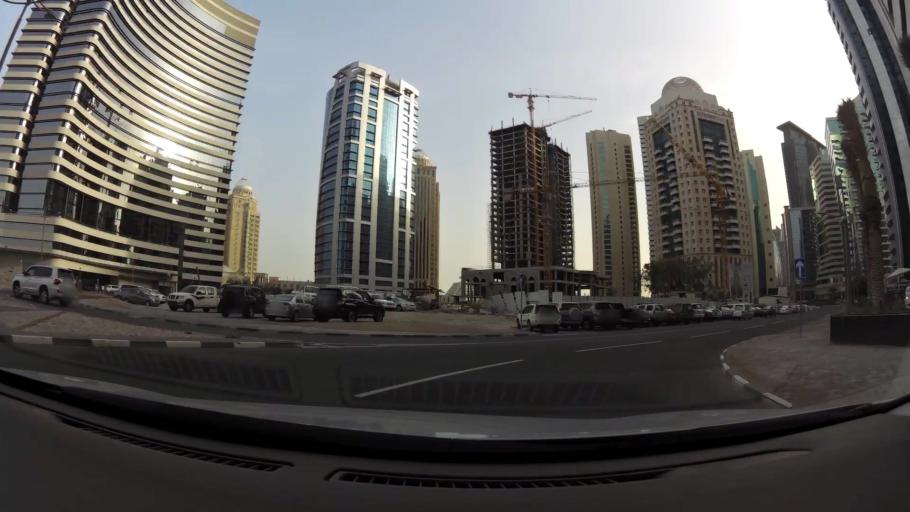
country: QA
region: Baladiyat ad Dawhah
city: Doha
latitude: 25.3270
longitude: 51.5378
